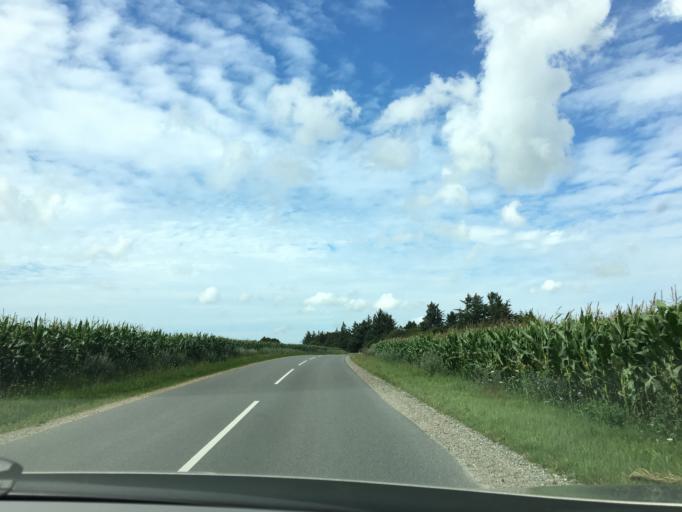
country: DK
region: South Denmark
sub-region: Varde Kommune
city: Oksbol
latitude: 55.7317
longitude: 8.2533
